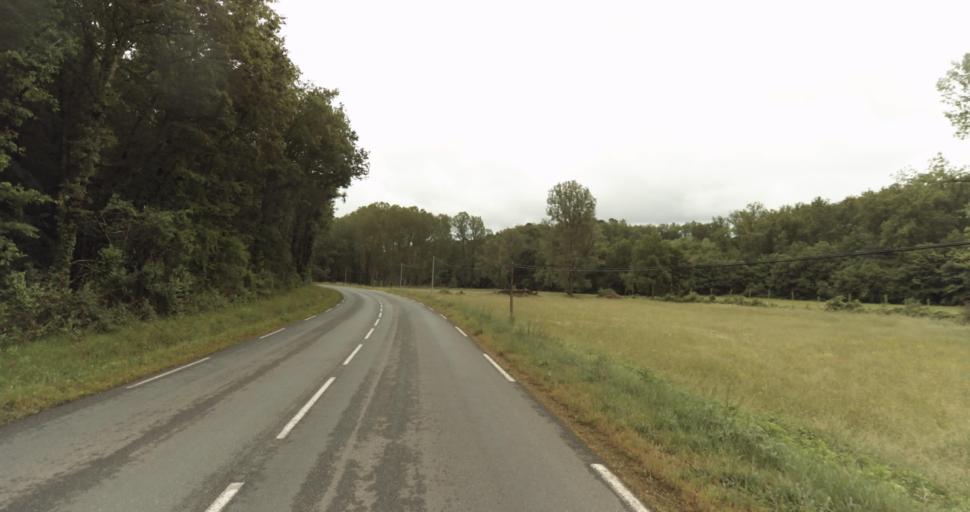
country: FR
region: Aquitaine
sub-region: Departement de la Dordogne
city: Belves
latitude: 44.6765
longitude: 0.9227
